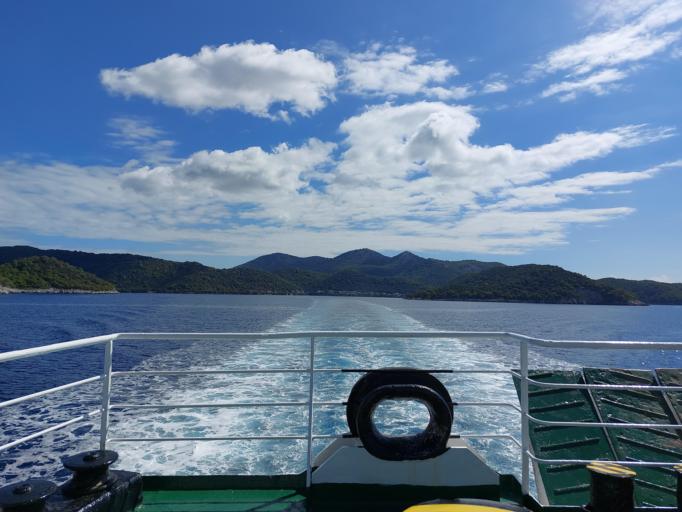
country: HR
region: Dubrovacko-Neretvanska
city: Smokvica
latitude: 42.7508
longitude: 16.8001
